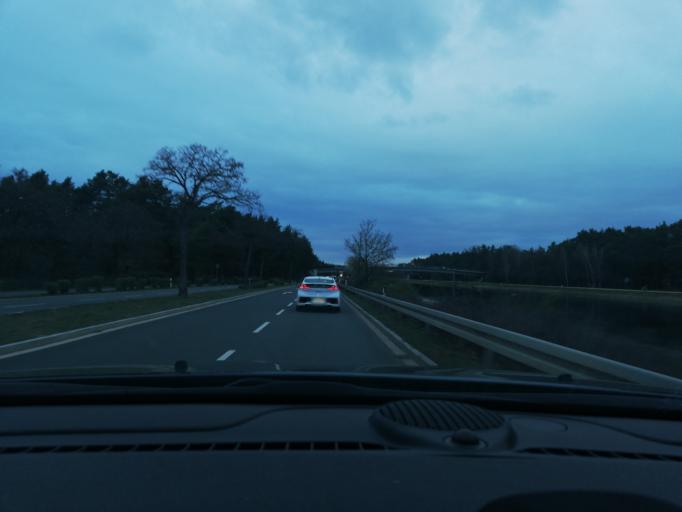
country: DE
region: Bavaria
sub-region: Regierungsbezirk Mittelfranken
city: Erlangen
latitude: 49.6056
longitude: 10.9717
